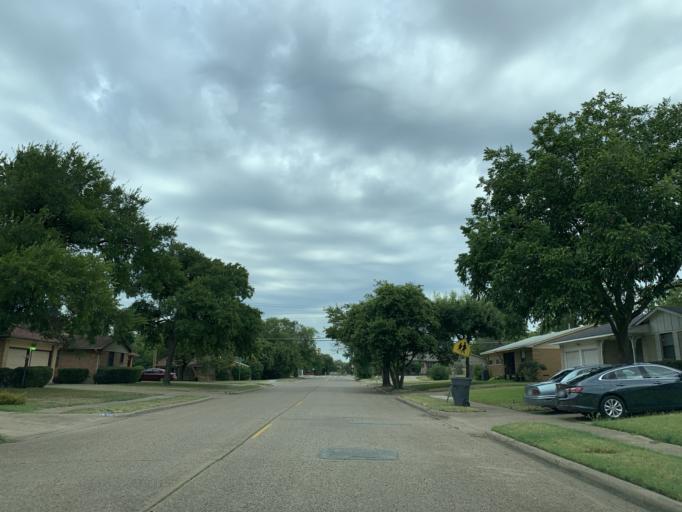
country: US
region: Texas
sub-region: Dallas County
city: DeSoto
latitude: 32.6610
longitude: -96.8309
